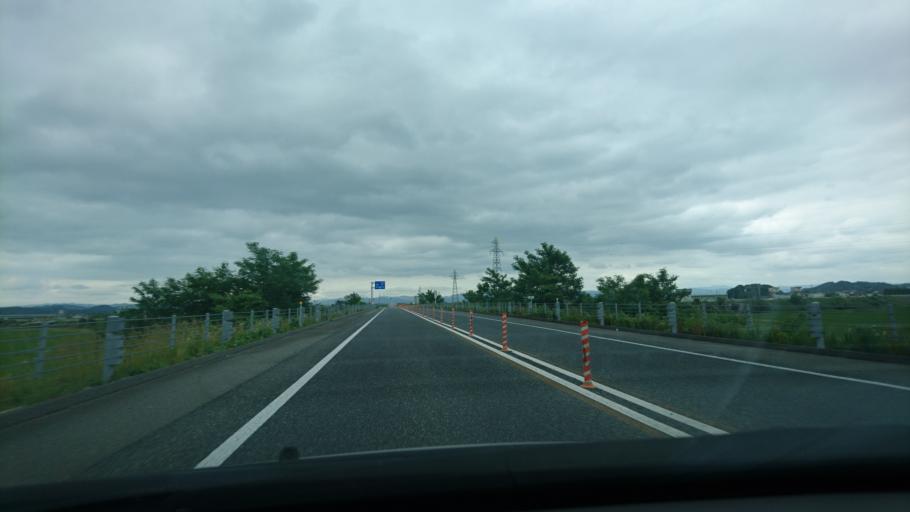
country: JP
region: Miyagi
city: Wakuya
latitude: 38.7274
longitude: 141.1457
